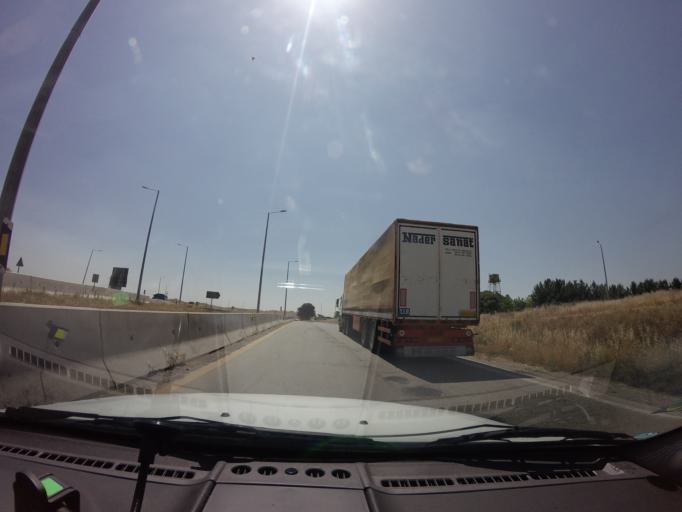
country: IR
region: Tehran
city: Eslamshahr
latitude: 35.4380
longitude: 51.2056
